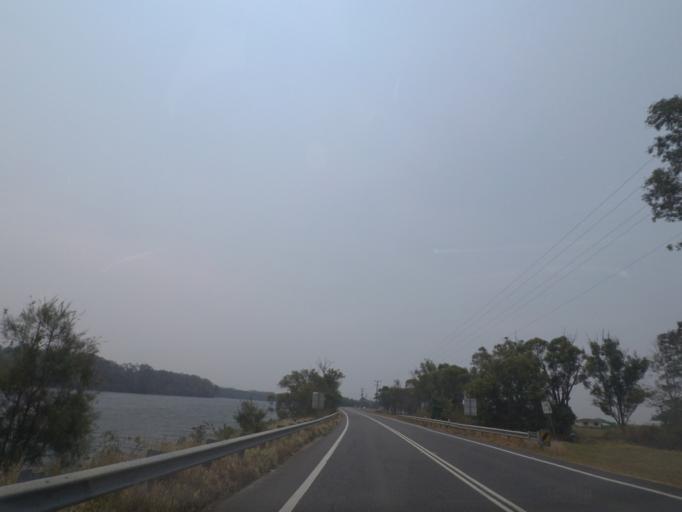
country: AU
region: New South Wales
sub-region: Richmond Valley
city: Evans Head
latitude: -28.9881
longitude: 153.4625
